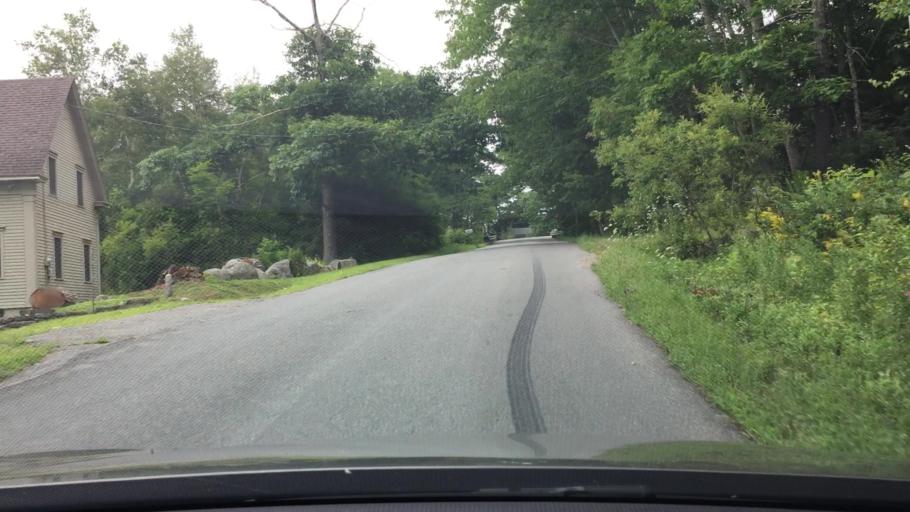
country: US
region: Maine
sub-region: Waldo County
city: Stockton Springs
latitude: 44.5071
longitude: -68.8158
